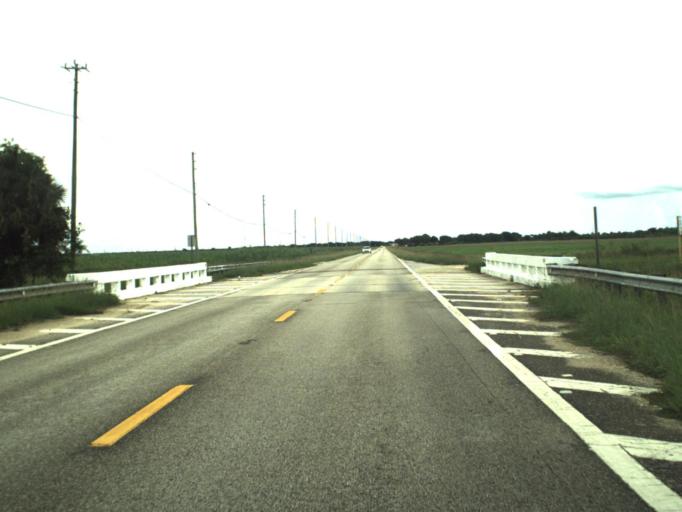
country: US
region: Florida
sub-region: Miami-Dade County
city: Florida City
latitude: 25.4077
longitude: -80.5240
